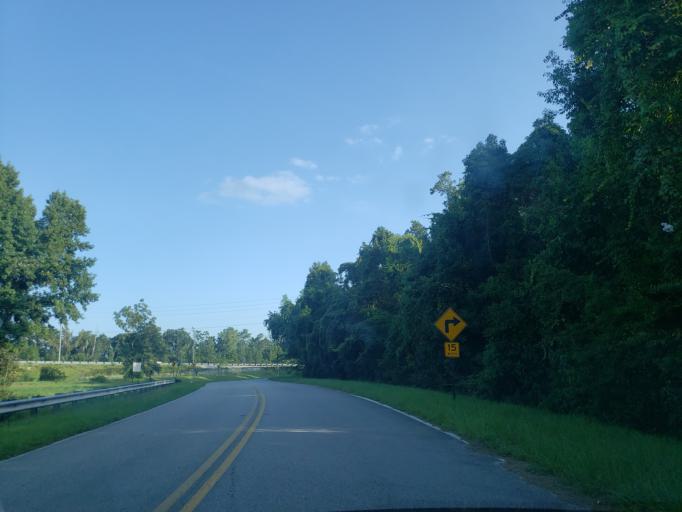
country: US
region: Georgia
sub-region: Chatham County
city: Isle of Hope
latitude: 31.9895
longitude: -81.0854
